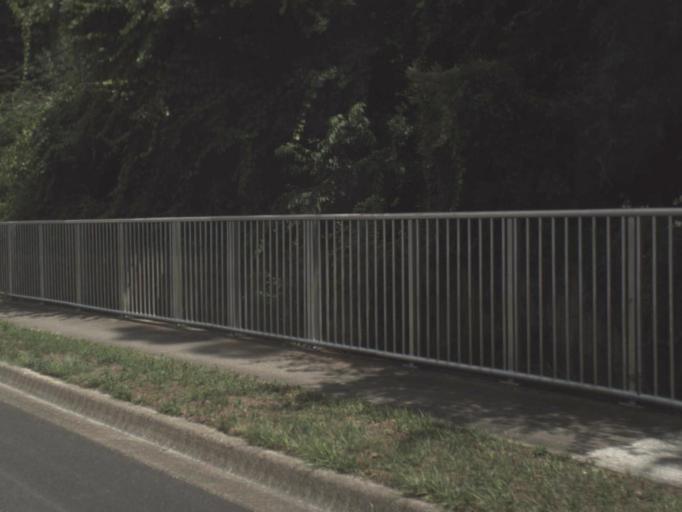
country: US
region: Florida
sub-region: Alachua County
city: Gainesville
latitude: 29.6884
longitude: -82.3551
